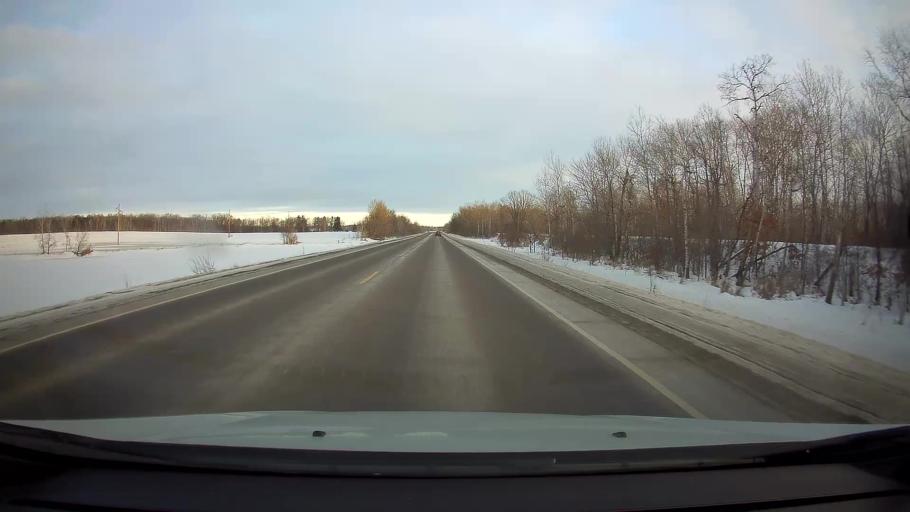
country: US
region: Wisconsin
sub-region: Polk County
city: Clear Lake
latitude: 45.2973
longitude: -92.2257
